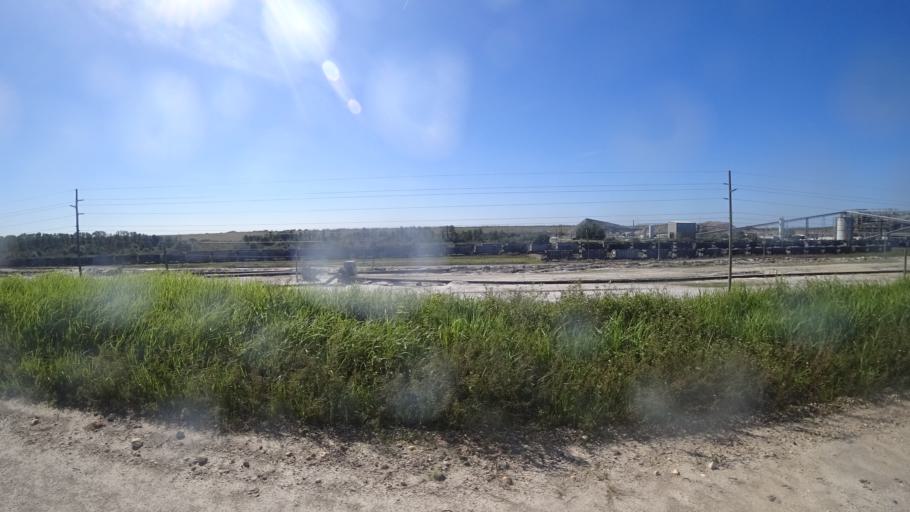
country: US
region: Florida
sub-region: Hillsborough County
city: Balm
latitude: 27.6490
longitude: -82.0822
